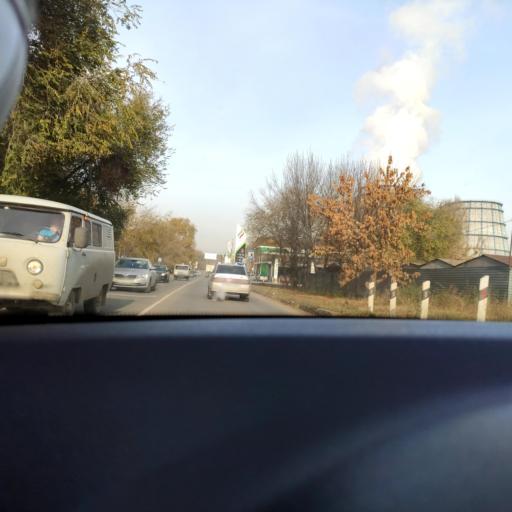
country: RU
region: Samara
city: Petra-Dubrava
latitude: 53.2463
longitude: 50.2697
